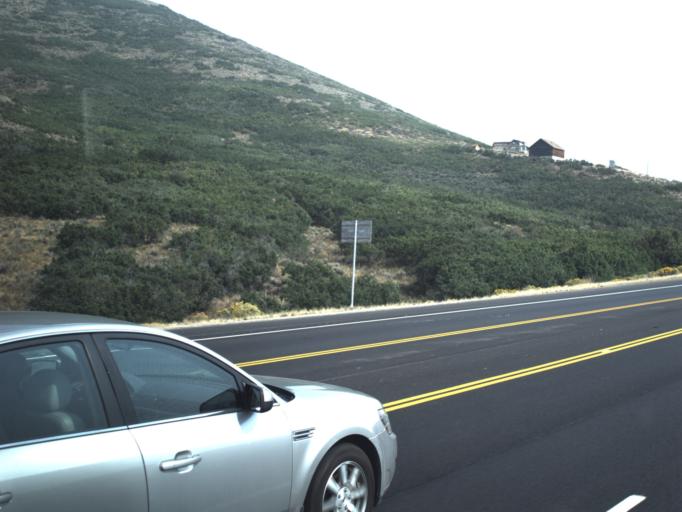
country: US
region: Utah
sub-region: Summit County
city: Park City
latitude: 40.6535
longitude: -111.4095
